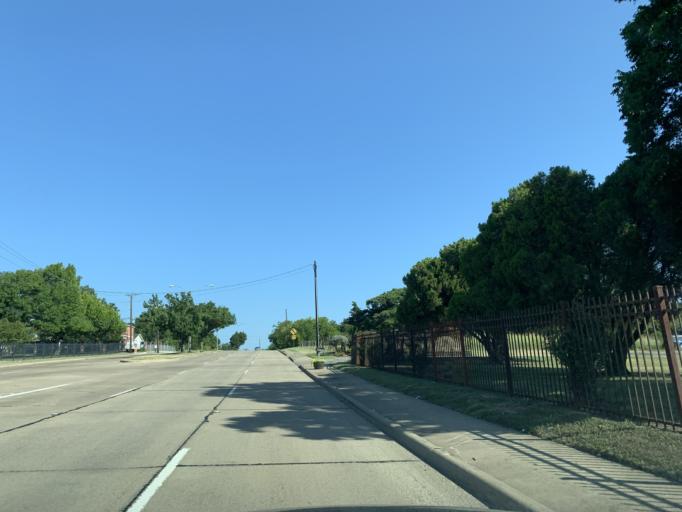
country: US
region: Texas
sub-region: Dallas County
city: Hutchins
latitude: 32.6604
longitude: -96.7525
